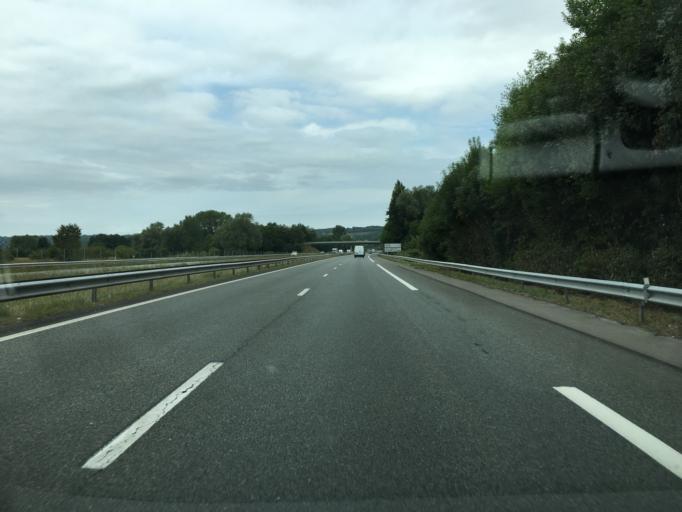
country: FR
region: Rhone-Alpes
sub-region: Departement de l'Isere
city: Saint-Jean-de-Moirans
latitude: 45.3269
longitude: 5.5970
